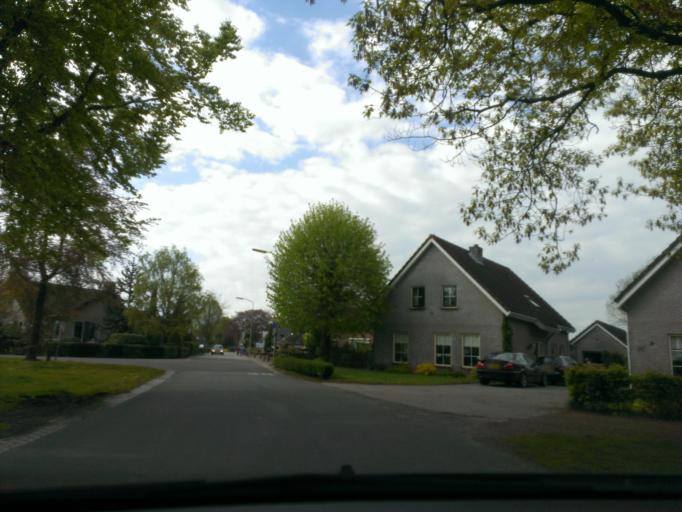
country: NL
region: Gelderland
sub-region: Gemeente Epe
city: Oene
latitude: 52.3412
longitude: 6.0514
